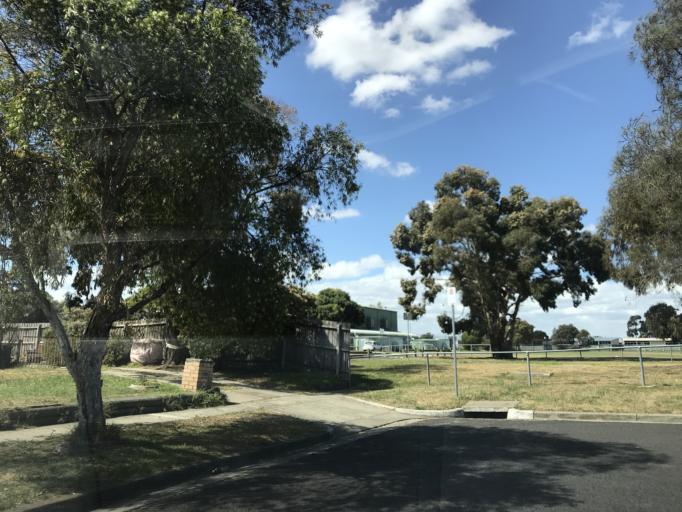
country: AU
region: Victoria
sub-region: Brimbank
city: Sunshine West
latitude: -37.7994
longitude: 144.8110
